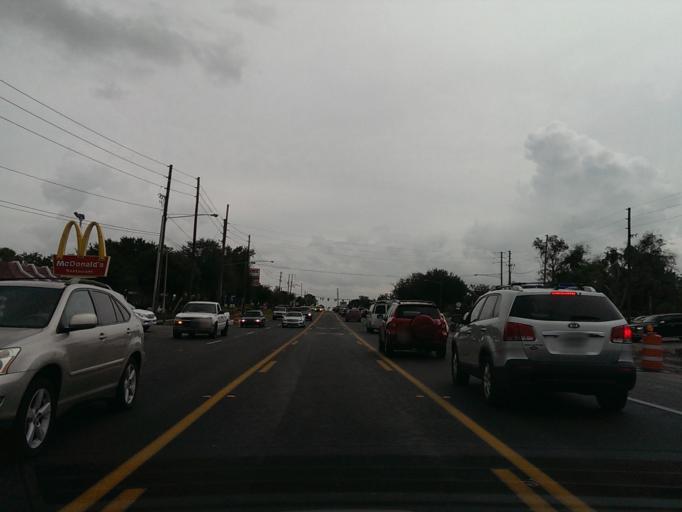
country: US
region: Florida
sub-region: Orange County
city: Ocoee
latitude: 28.5516
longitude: -81.5452
